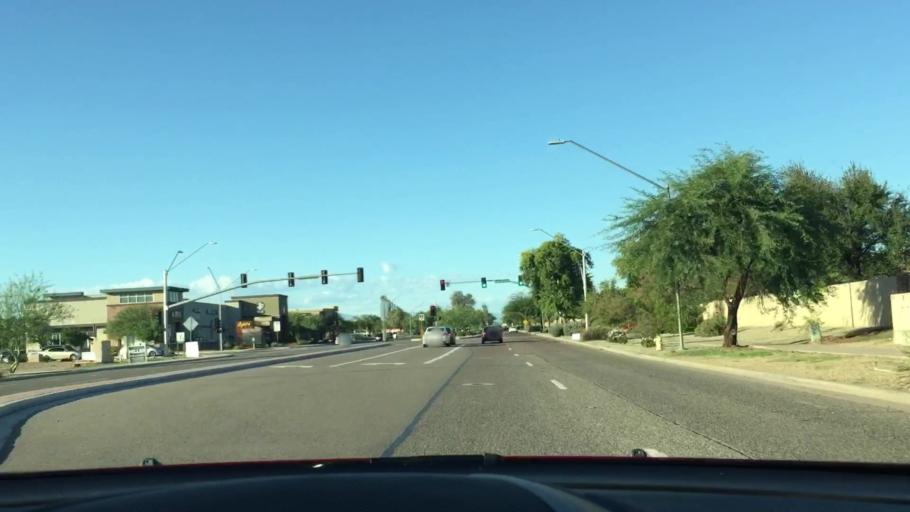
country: US
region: Arizona
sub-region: Maricopa County
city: Sun City
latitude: 33.6699
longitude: -112.2203
